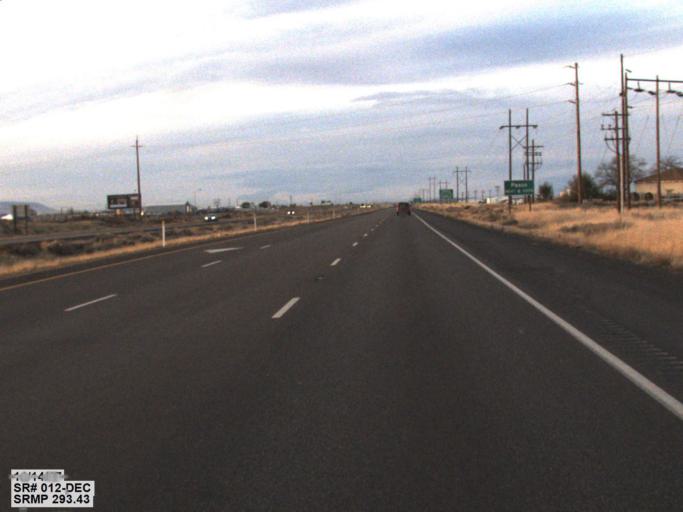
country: US
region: Washington
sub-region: Walla Walla County
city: Burbank
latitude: 46.2290
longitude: -119.0414
